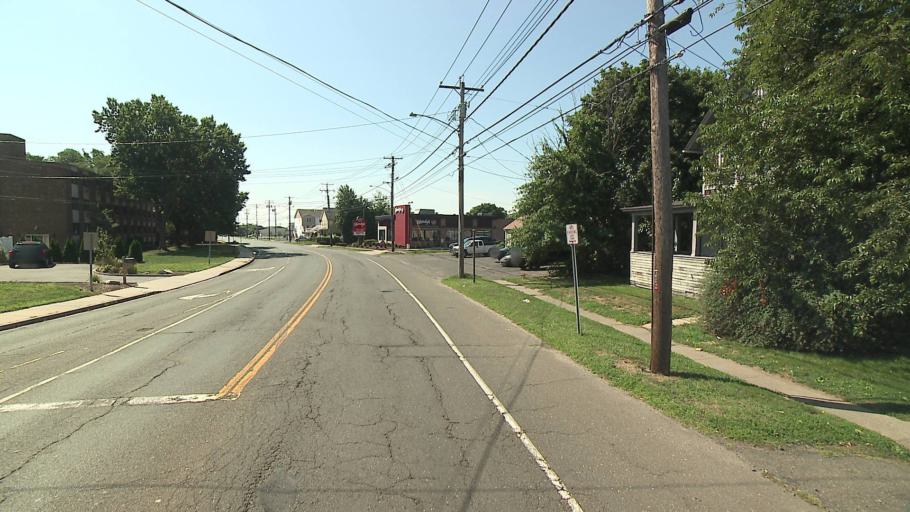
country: US
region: Connecticut
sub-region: Fairfield County
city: Stratford
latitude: 41.1764
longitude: -73.1302
